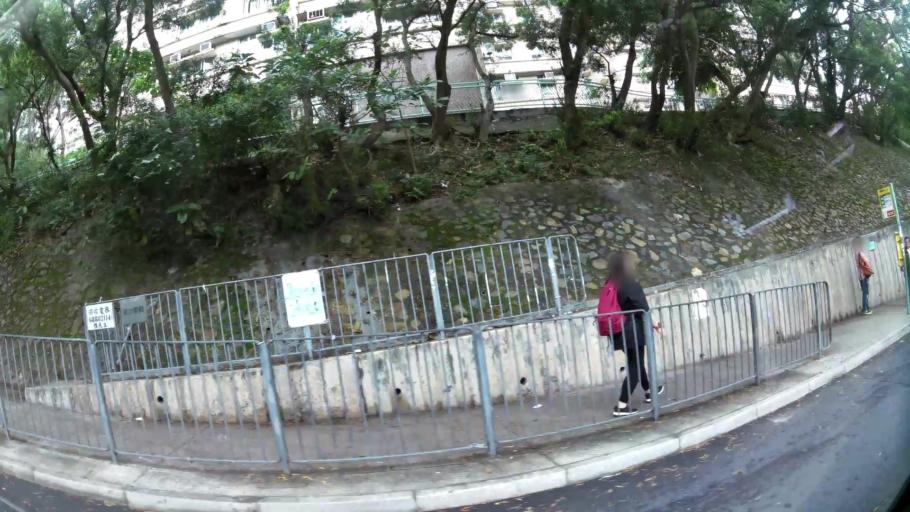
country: HK
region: Central and Western
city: Central
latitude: 22.2427
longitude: 114.1579
